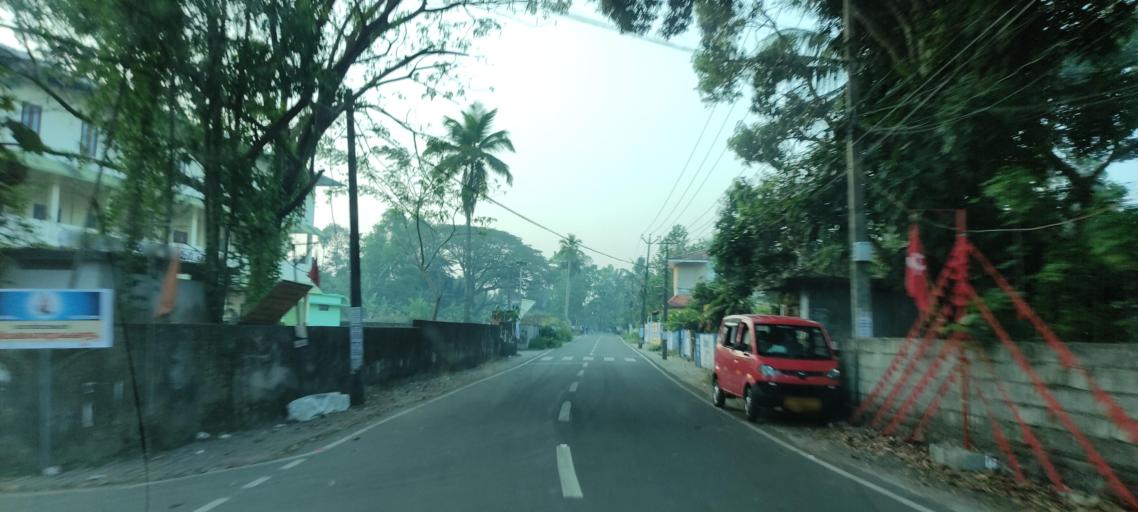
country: IN
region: Kerala
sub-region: Alappuzha
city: Alleppey
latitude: 9.4533
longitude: 76.3449
